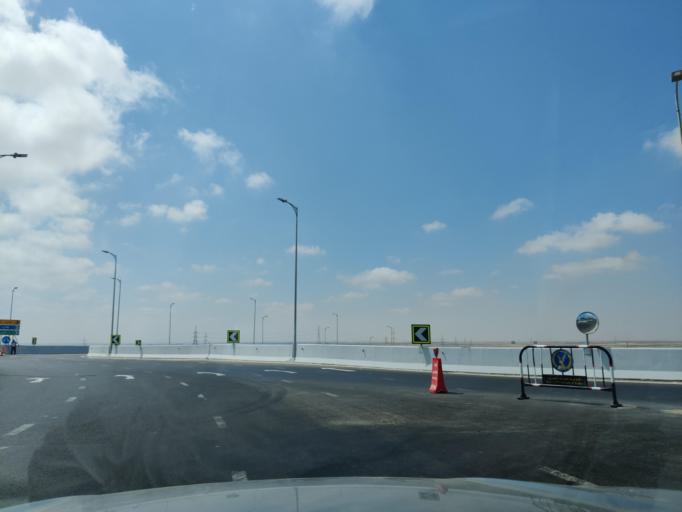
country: EG
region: Muhafazat Matruh
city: Al `Alamayn
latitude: 30.8239
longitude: 28.9854
